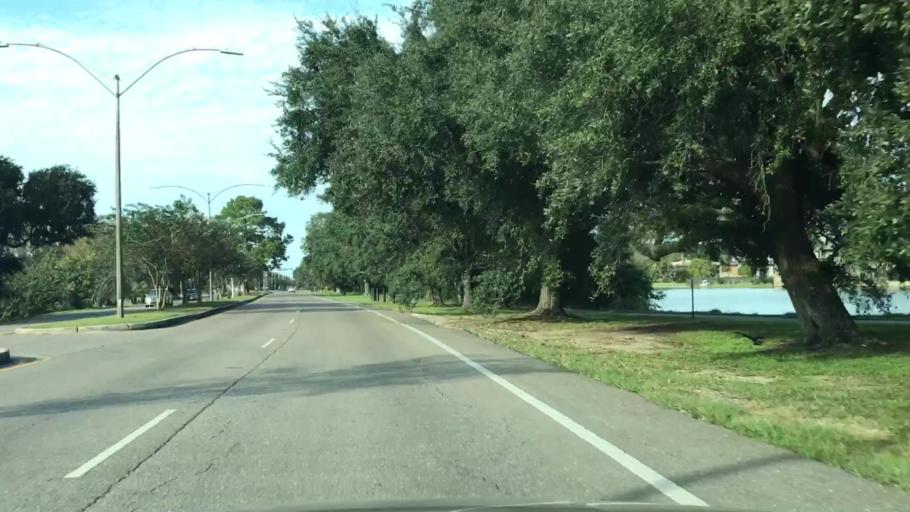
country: US
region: Louisiana
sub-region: Orleans Parish
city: New Orleans
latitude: 29.9970
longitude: -90.0859
